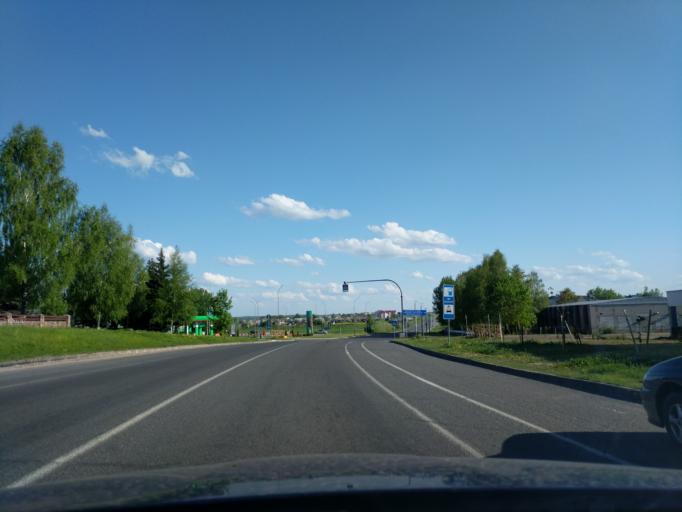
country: BY
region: Minsk
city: Myadzyel
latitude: 54.8842
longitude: 26.9380
